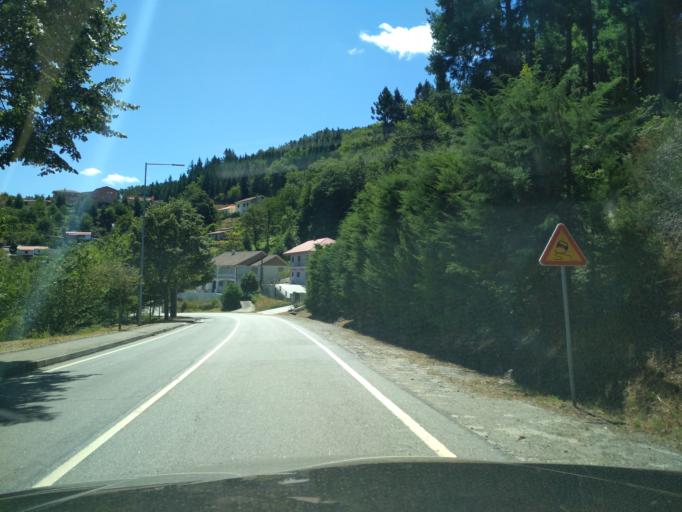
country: PT
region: Vila Real
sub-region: Ribeira de Pena
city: Ribeira de Pena
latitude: 41.5189
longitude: -7.8060
